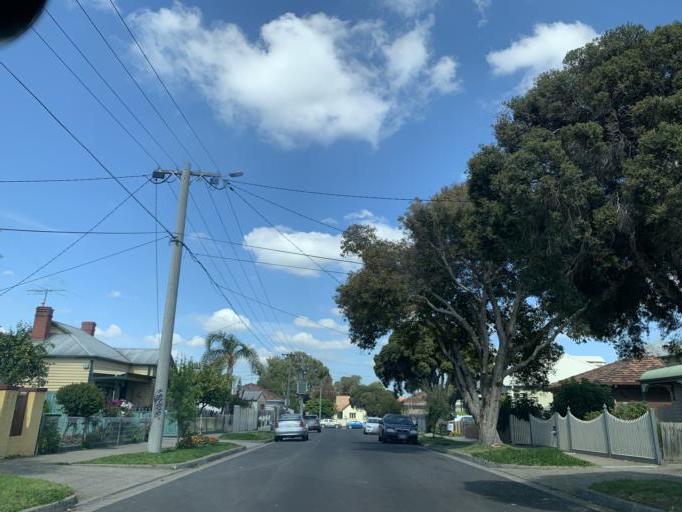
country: AU
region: Victoria
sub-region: Moreland
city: Coburg North
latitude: -37.7358
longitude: 144.9573
